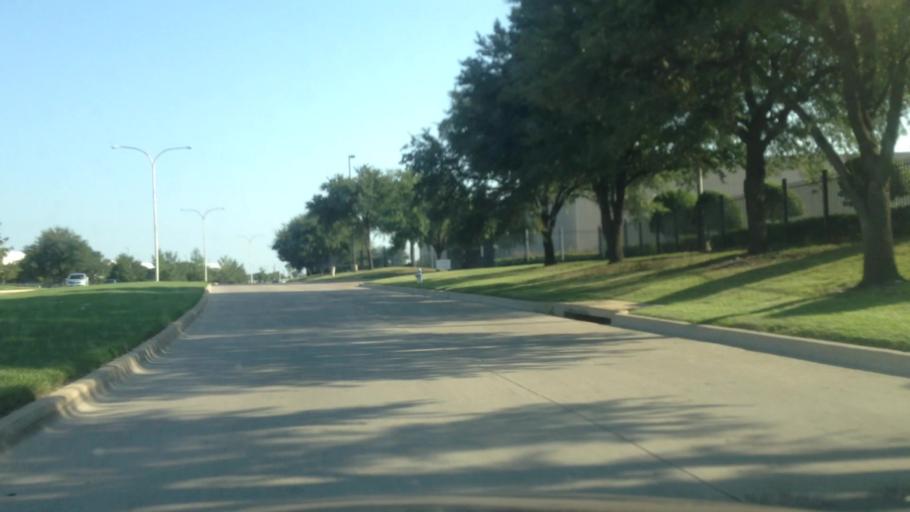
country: US
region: Texas
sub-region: Tarrant County
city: Haltom City
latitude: 32.8198
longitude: -97.3085
